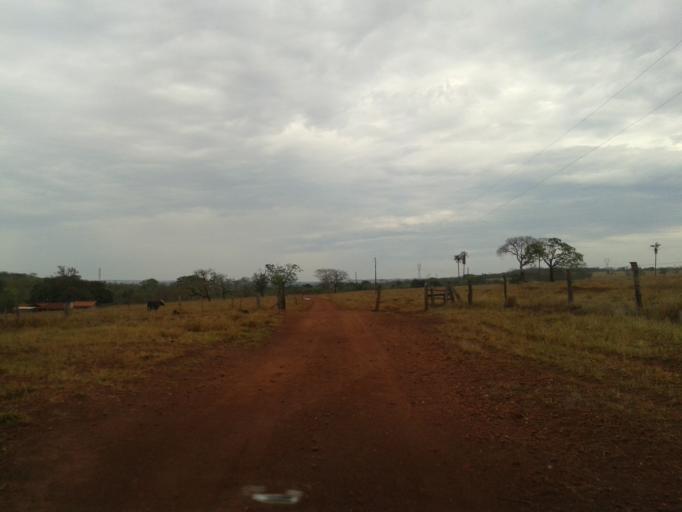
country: BR
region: Minas Gerais
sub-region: Santa Vitoria
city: Santa Vitoria
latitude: -18.8524
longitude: -49.8288
